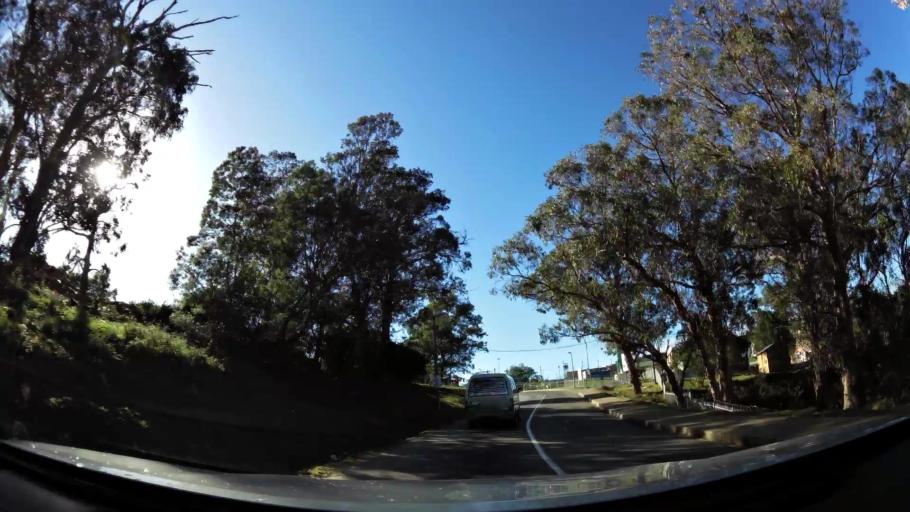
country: ZA
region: Western Cape
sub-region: Eden District Municipality
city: Knysna
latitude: -34.0271
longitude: 23.0535
